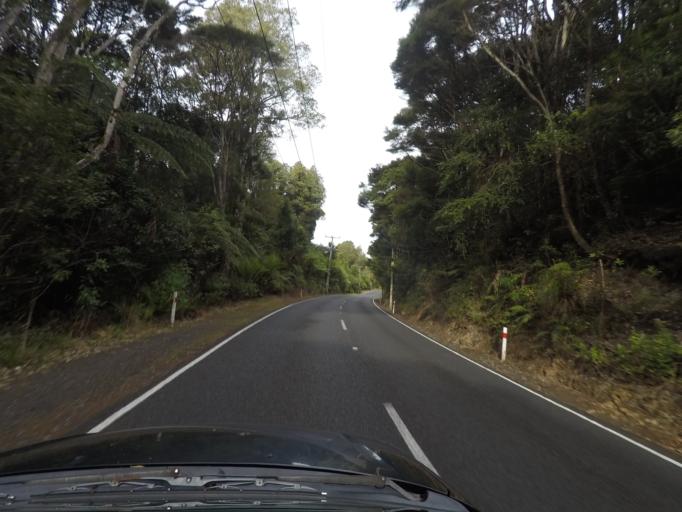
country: NZ
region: Auckland
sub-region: Auckland
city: Titirangi
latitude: -36.9399
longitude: 174.5822
